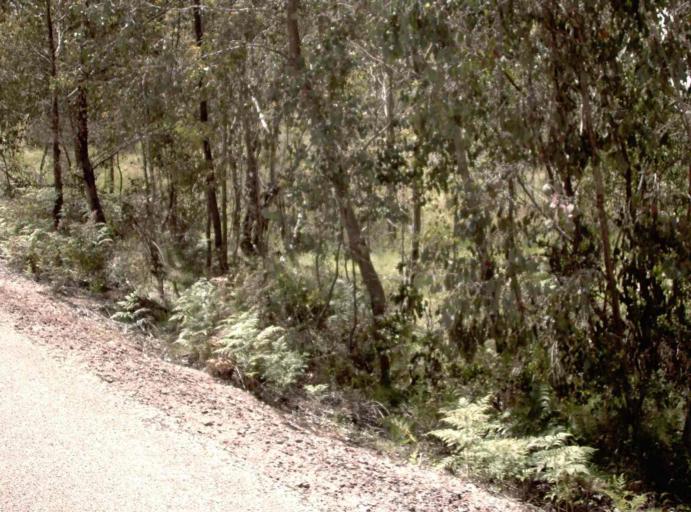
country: AU
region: New South Wales
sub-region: Snowy River
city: Jindabyne
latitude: -37.1133
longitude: 148.2473
